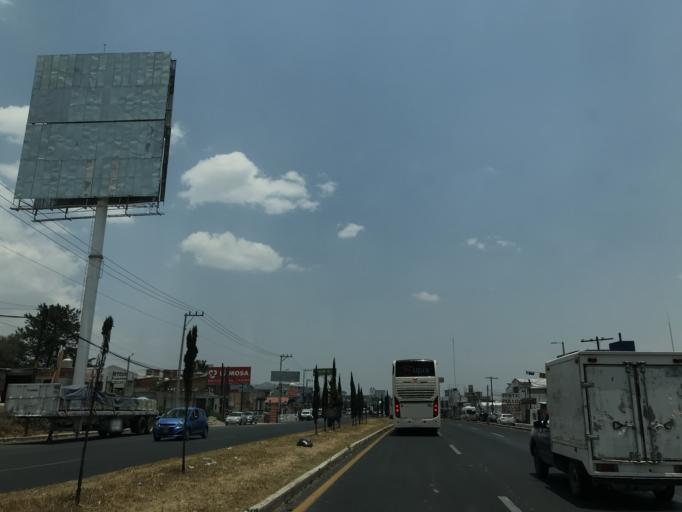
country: MX
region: Tlaxcala
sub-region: Yauhquemehcan
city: Hualcaltzinco
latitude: 19.4138
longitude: -98.1625
